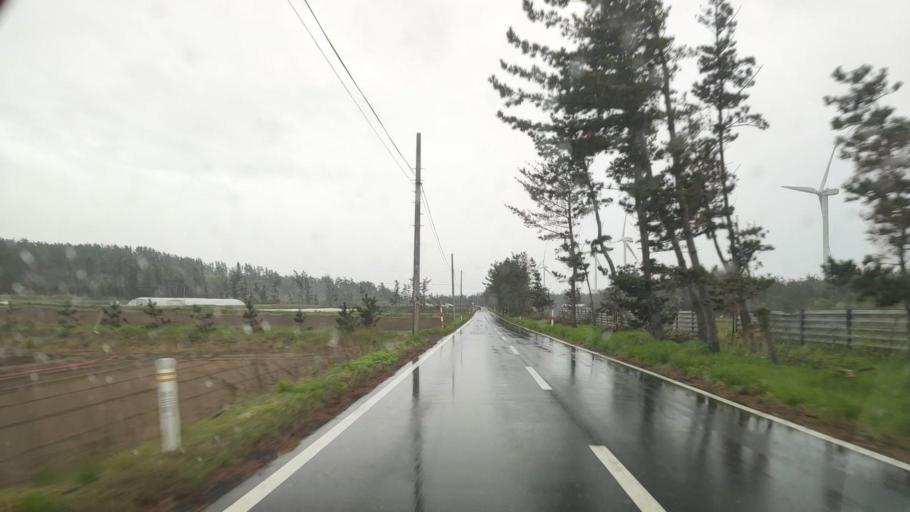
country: JP
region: Akita
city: Noshiromachi
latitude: 40.0745
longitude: 139.9511
